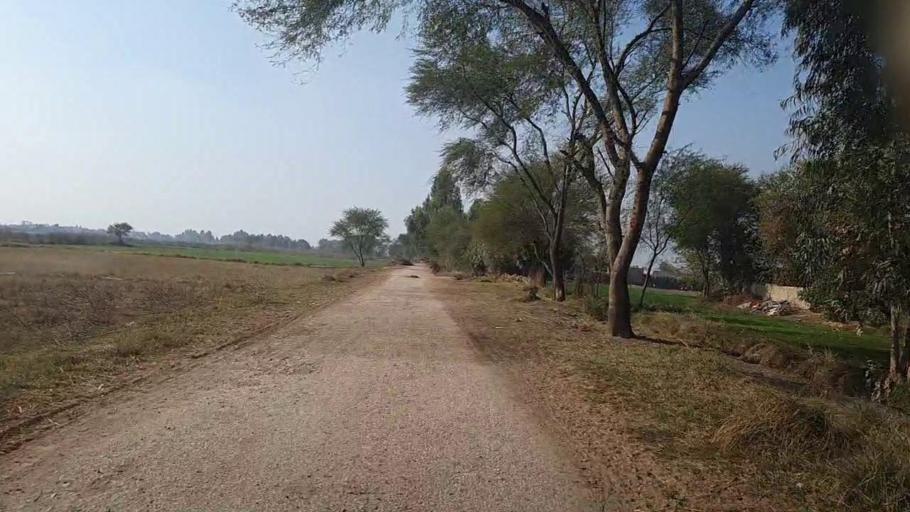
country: PK
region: Sindh
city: Mirpur Mathelo
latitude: 27.9022
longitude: 69.6333
